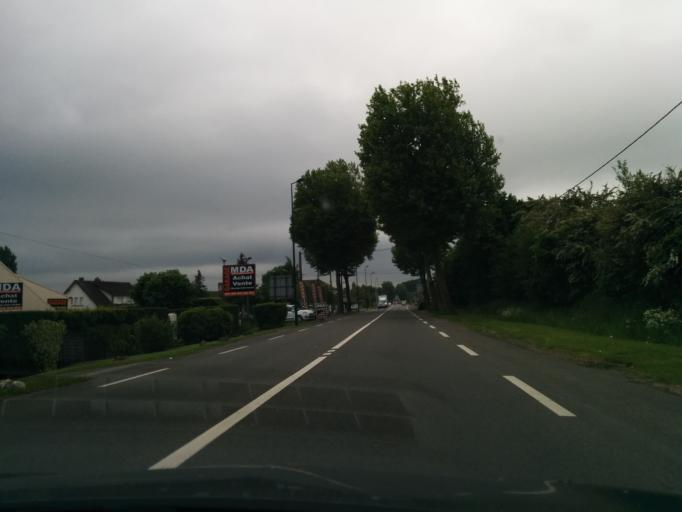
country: FR
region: Ile-de-France
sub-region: Departement des Yvelines
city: Freneuse
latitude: 49.0321
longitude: 1.6035
